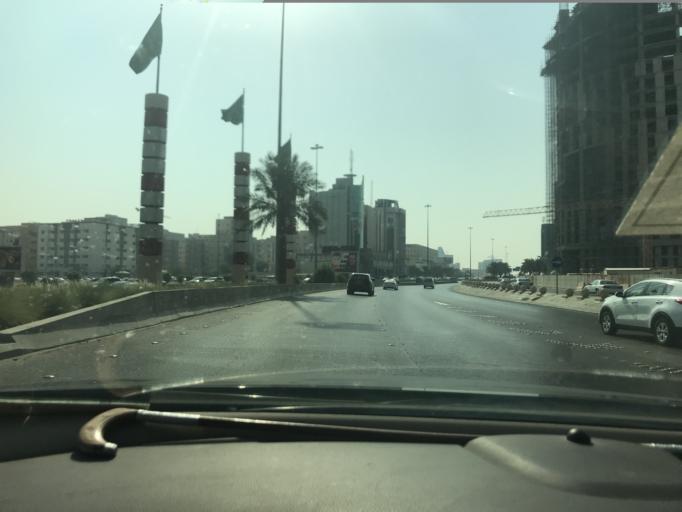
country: SA
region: Ar Riyad
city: Riyadh
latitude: 24.6768
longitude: 46.6892
